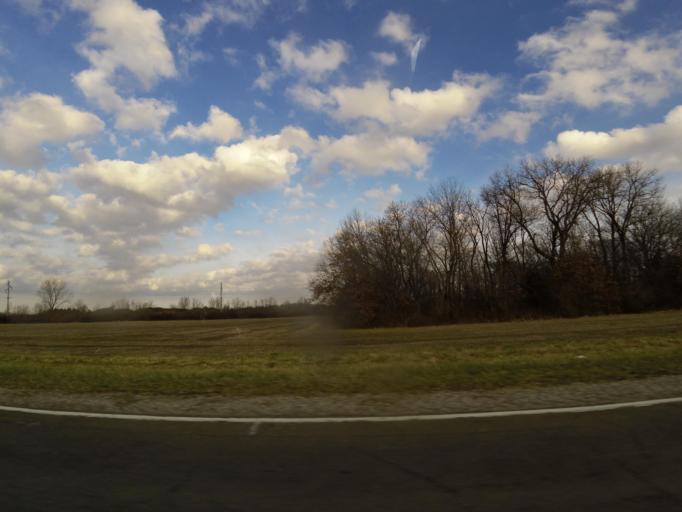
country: US
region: Illinois
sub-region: Bond County
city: Greenville
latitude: 38.9184
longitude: -89.2821
